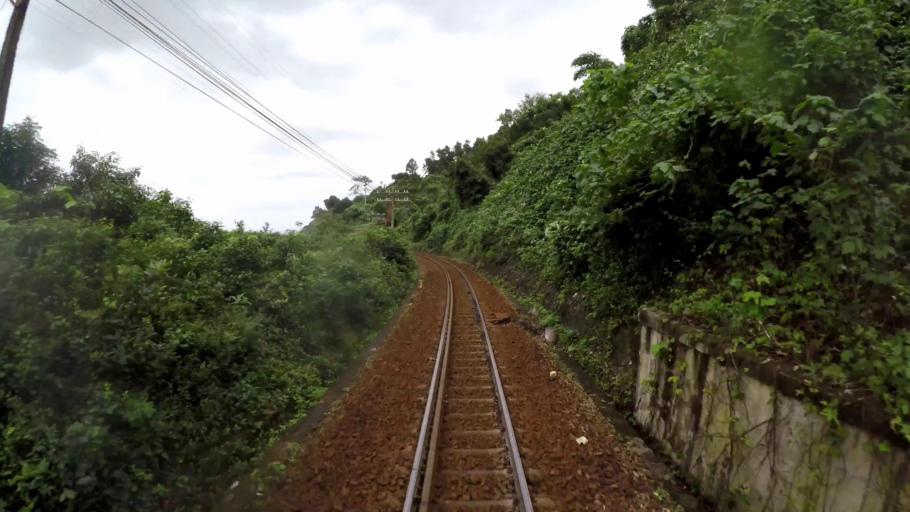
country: VN
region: Da Nang
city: Lien Chieu
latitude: 16.1597
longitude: 108.1346
